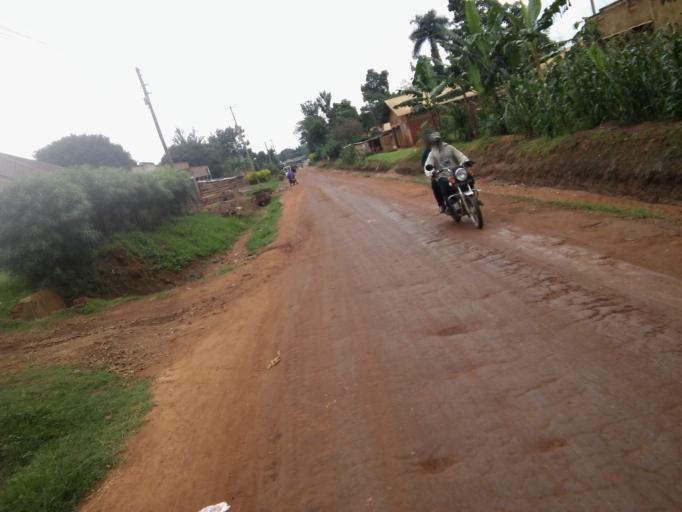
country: UG
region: Eastern Region
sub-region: Mbale District
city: Mbale
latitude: 1.0395
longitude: 34.1815
